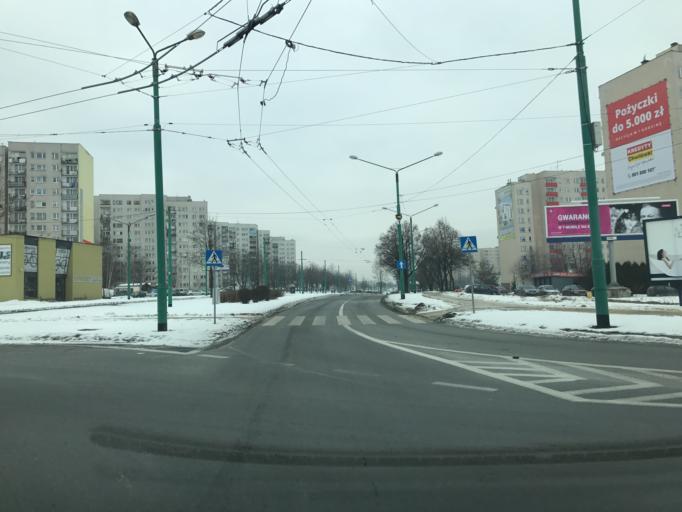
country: PL
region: Silesian Voivodeship
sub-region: Tychy
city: Cielmice
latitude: 50.1035
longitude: 18.9953
